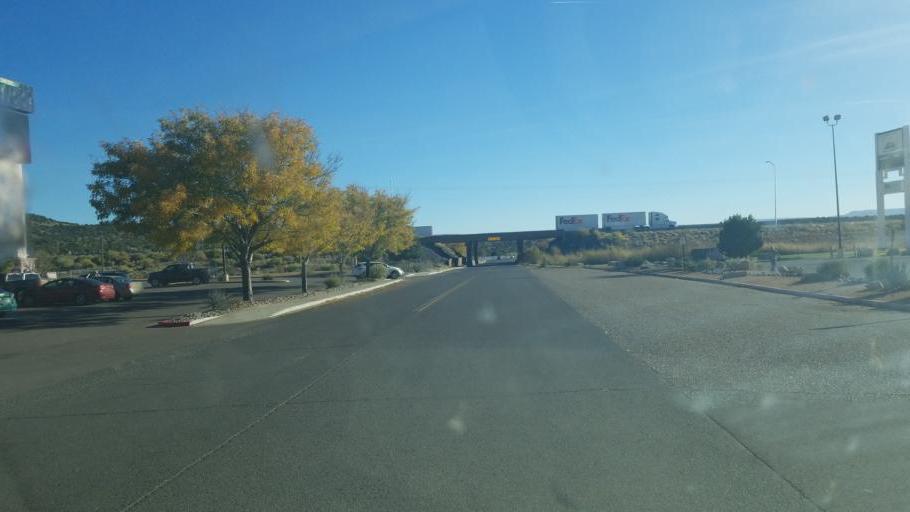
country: US
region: New Mexico
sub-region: Cibola County
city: Skyline-Ganipa
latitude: 35.0756
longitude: -107.5561
